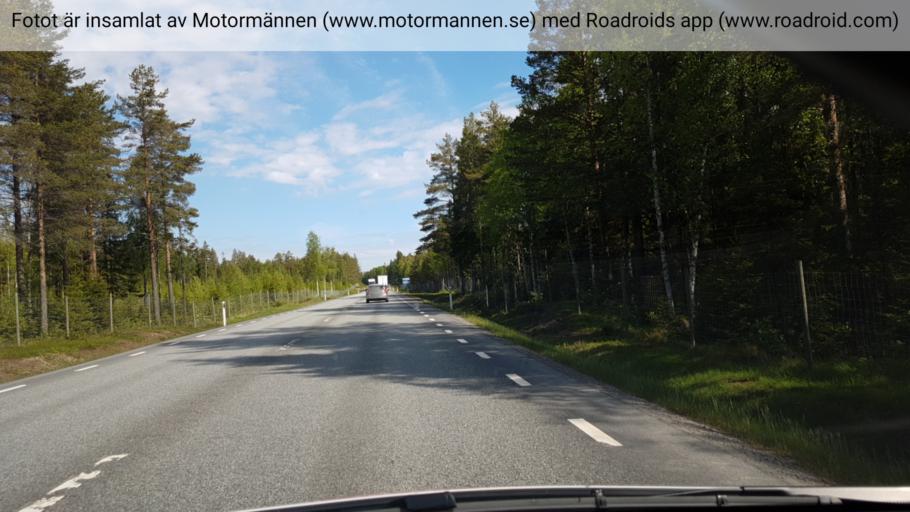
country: SE
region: Vaesterbotten
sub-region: Skelleftea Kommun
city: Burea
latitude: 64.5293
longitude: 21.2581
